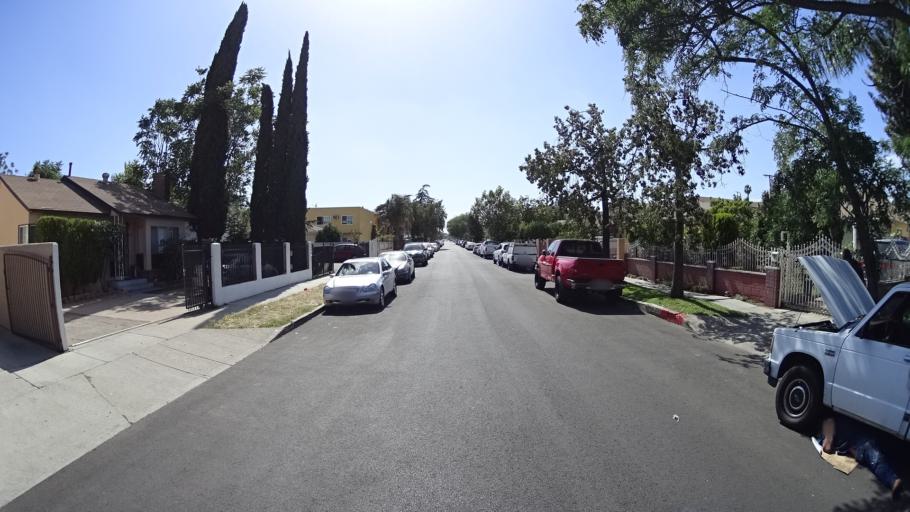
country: US
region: California
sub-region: Los Angeles County
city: North Hollywood
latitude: 34.1785
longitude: -118.3768
